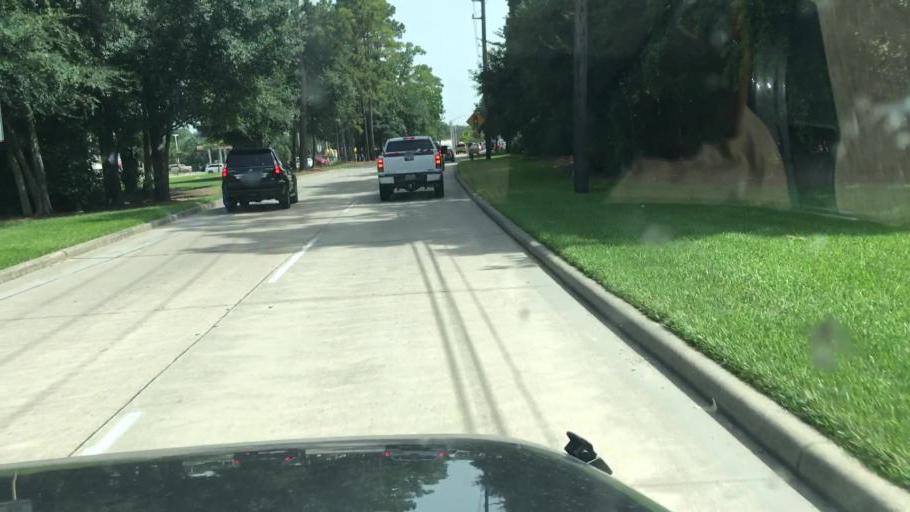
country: US
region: Texas
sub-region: Harris County
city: Atascocita
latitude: 29.9327
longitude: -95.1766
